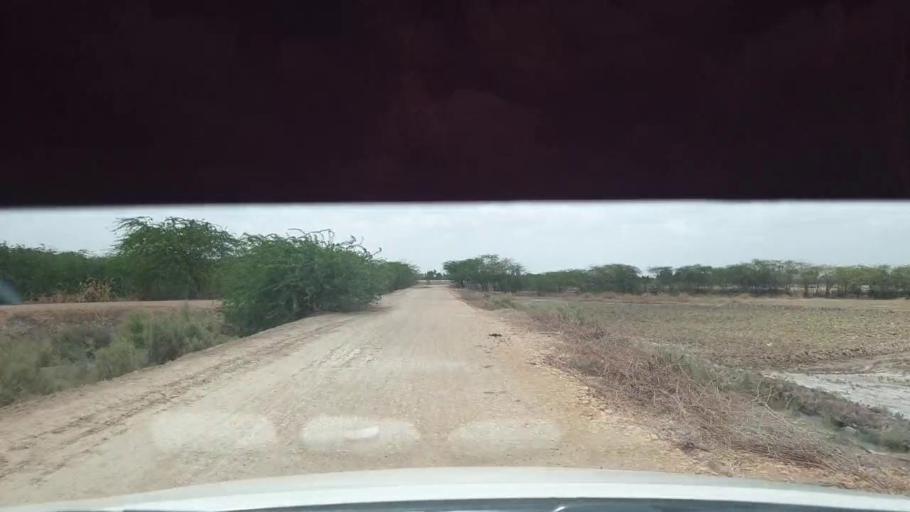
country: PK
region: Sindh
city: Kadhan
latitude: 24.4837
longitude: 68.9985
